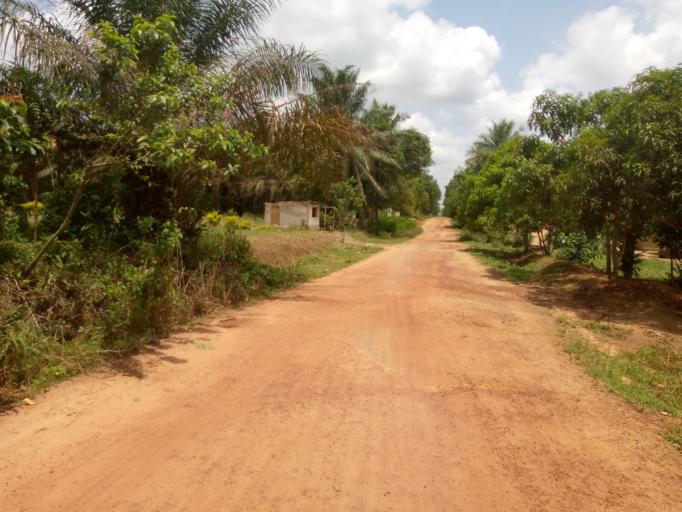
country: SL
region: Western Area
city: Waterloo
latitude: 8.3798
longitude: -12.9705
